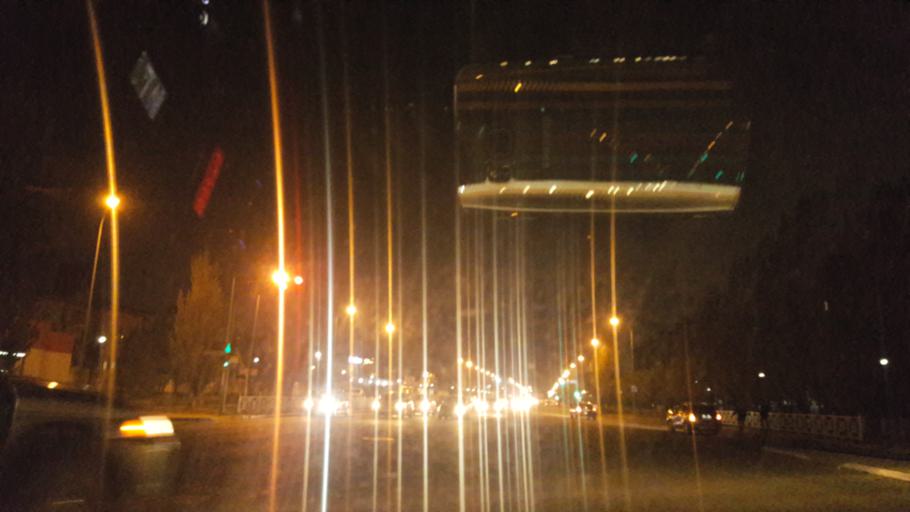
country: KZ
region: Astana Qalasy
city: Astana
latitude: 51.1527
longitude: 71.5087
